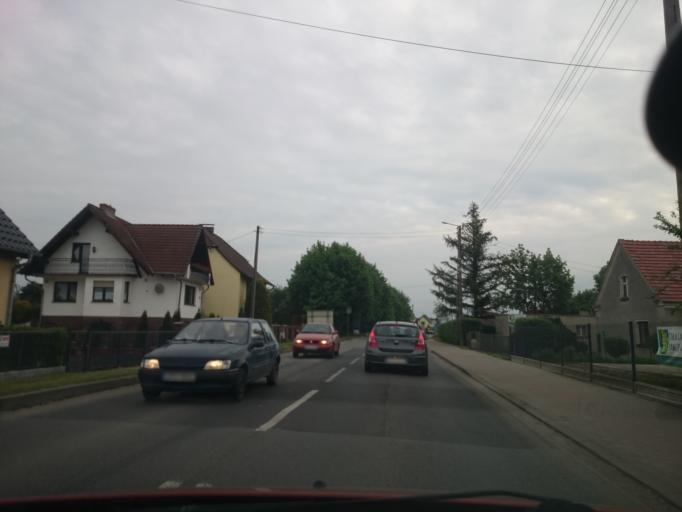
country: PL
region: Opole Voivodeship
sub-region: Powiat opolski
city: Dobrzen Wielki
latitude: 50.7678
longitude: 17.8470
